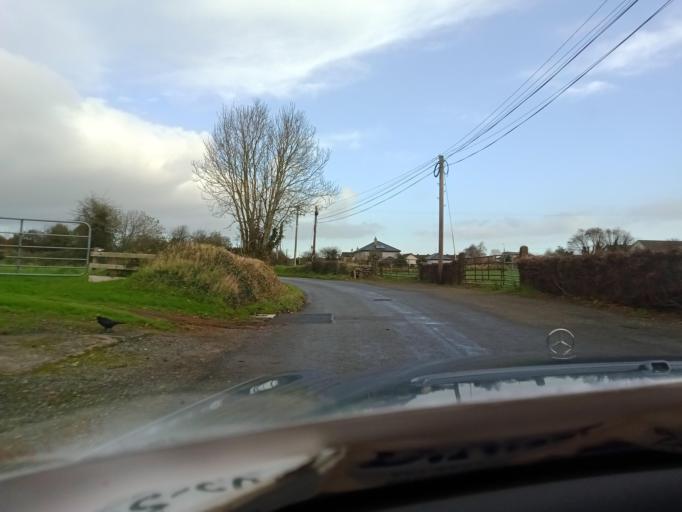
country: IE
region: Leinster
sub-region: Kilkenny
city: Mooncoin
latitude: 52.2893
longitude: -7.2518
